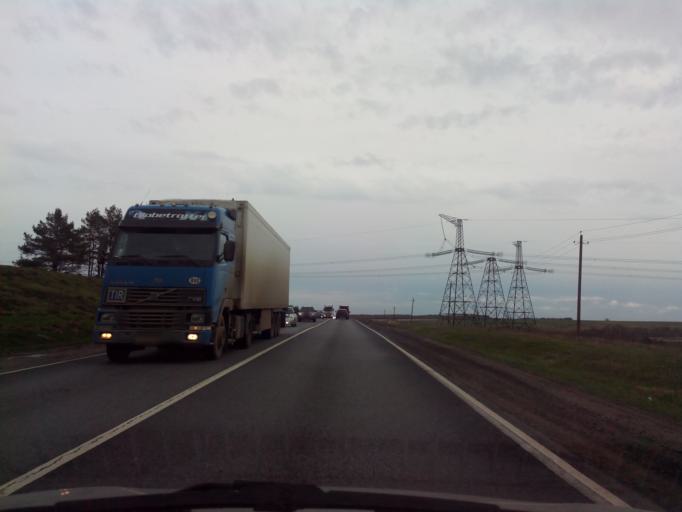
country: RU
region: Moskovskaya
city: Ozherel'ye
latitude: 54.7282
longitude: 38.2671
